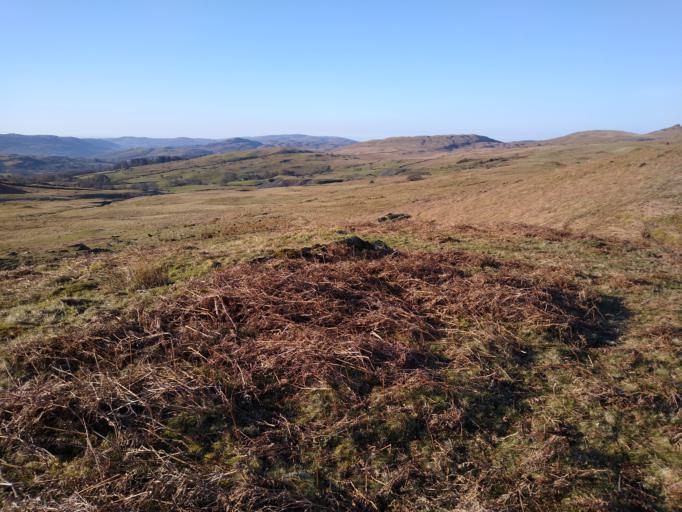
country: GB
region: England
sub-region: Cumbria
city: Ambleside
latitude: 54.3606
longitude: -3.1071
